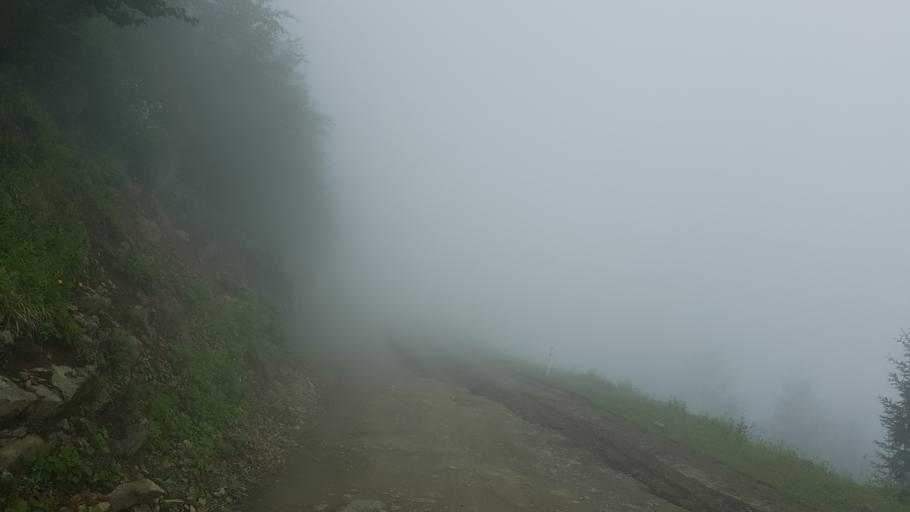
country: GE
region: Guria
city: Ozurgeti
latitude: 41.8341
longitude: 42.1546
